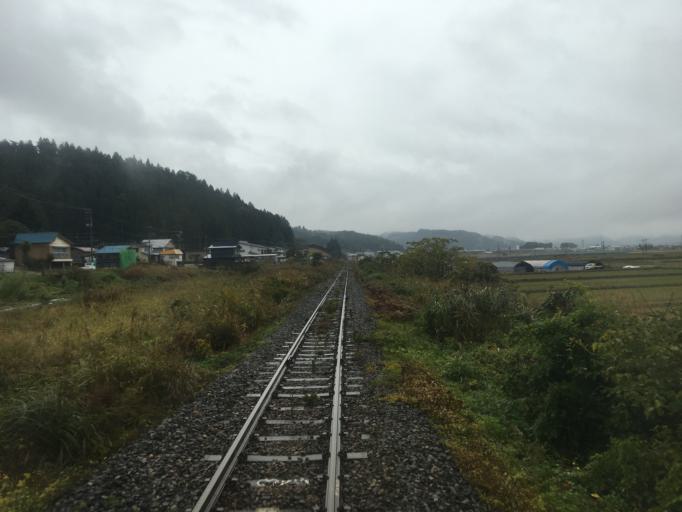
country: JP
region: Yamagata
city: Obanazawa
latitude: 38.7650
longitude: 140.5000
